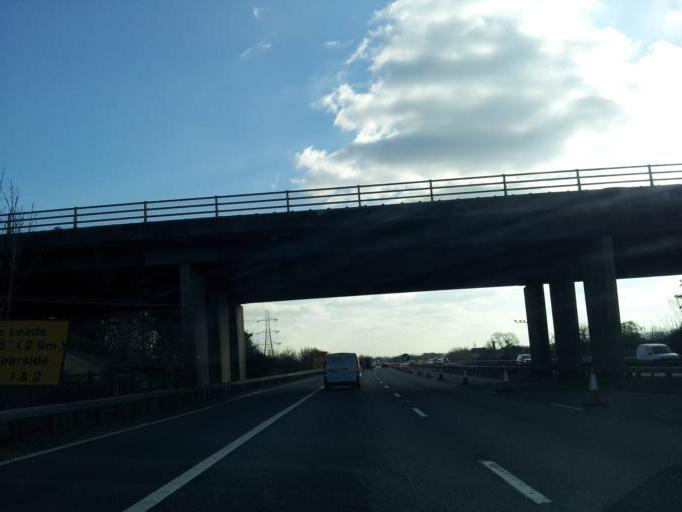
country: GB
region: England
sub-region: Somerset
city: Bridgwater
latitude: 51.1242
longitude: -2.9702
